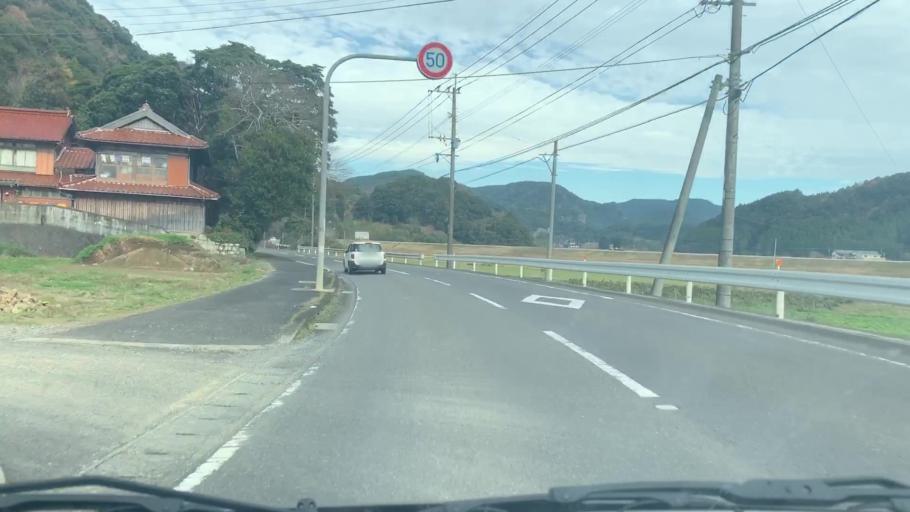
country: JP
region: Saga Prefecture
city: Imaricho-ko
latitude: 33.3152
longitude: 129.9704
